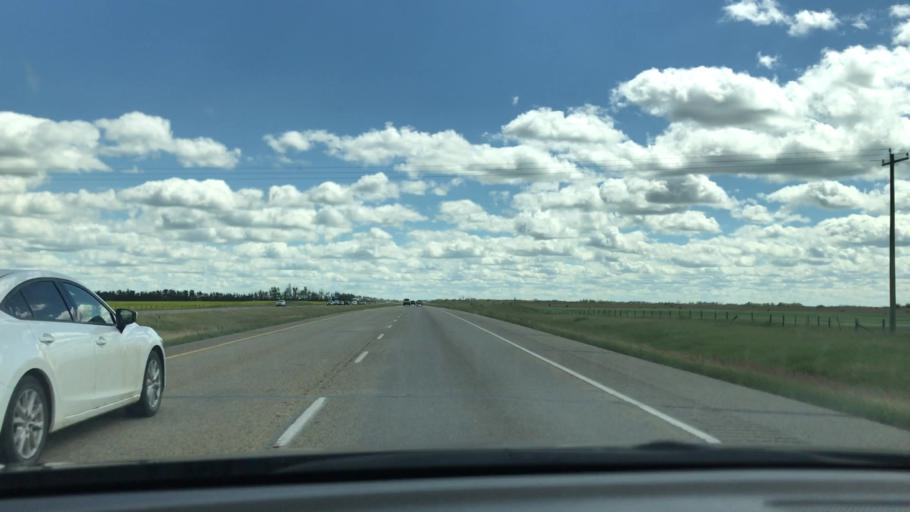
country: CA
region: Alberta
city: Leduc
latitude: 53.1638
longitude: -113.5984
